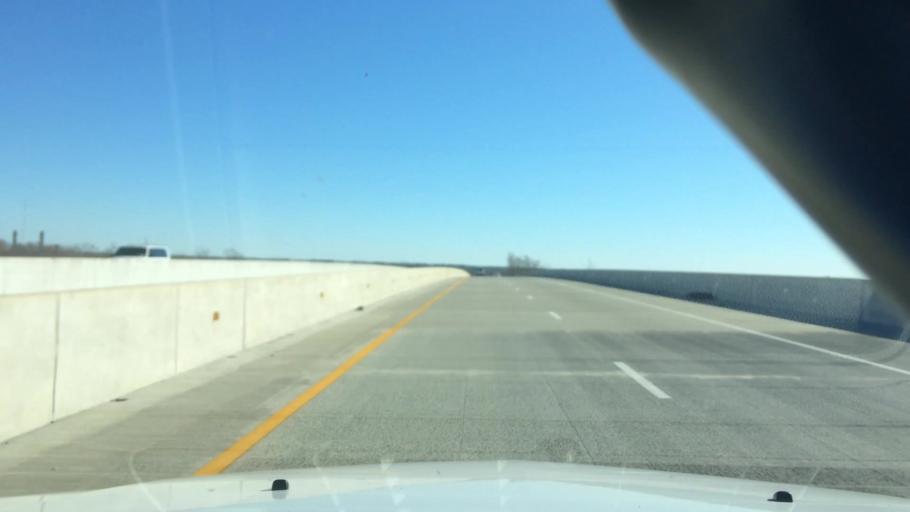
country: US
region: North Carolina
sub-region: Brunswick County
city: Navassa
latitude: 34.2731
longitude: -78.0031
